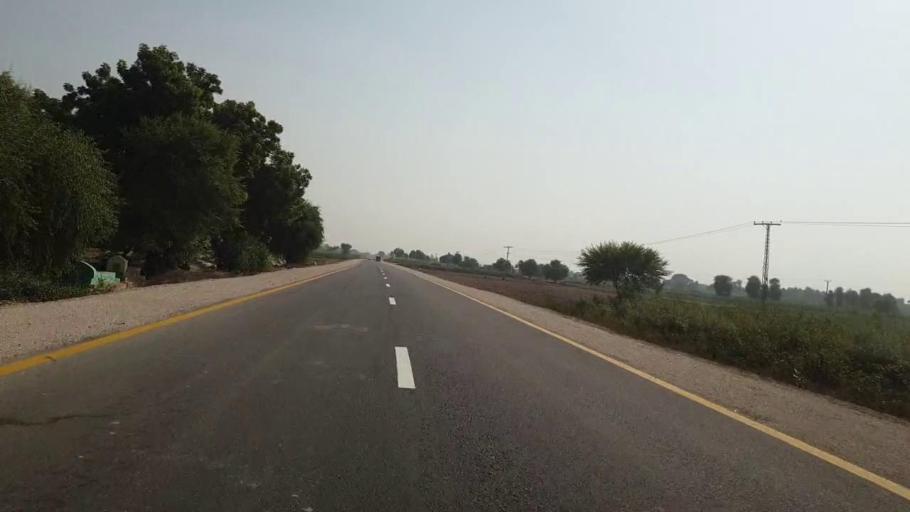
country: PK
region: Sindh
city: Bhan
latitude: 26.6145
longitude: 67.7783
